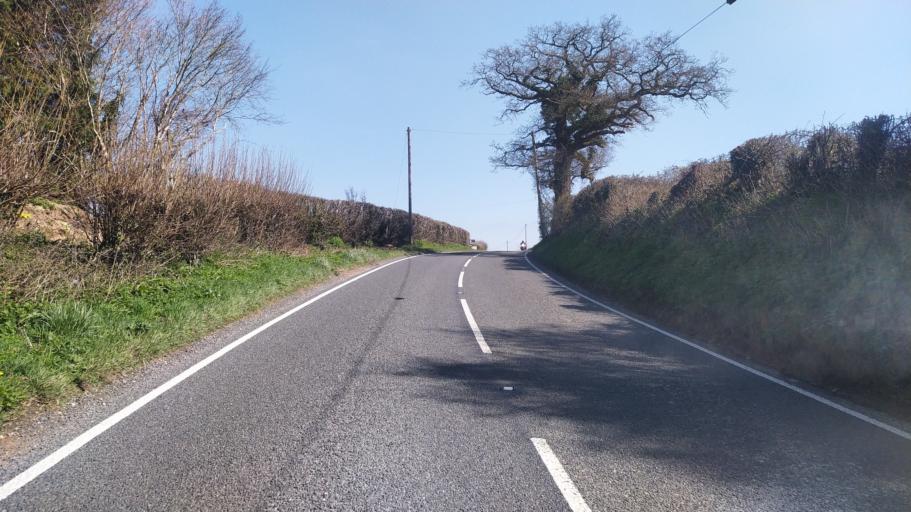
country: GB
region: England
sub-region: Dorset
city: Bovington Camp
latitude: 50.7742
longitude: -2.2931
